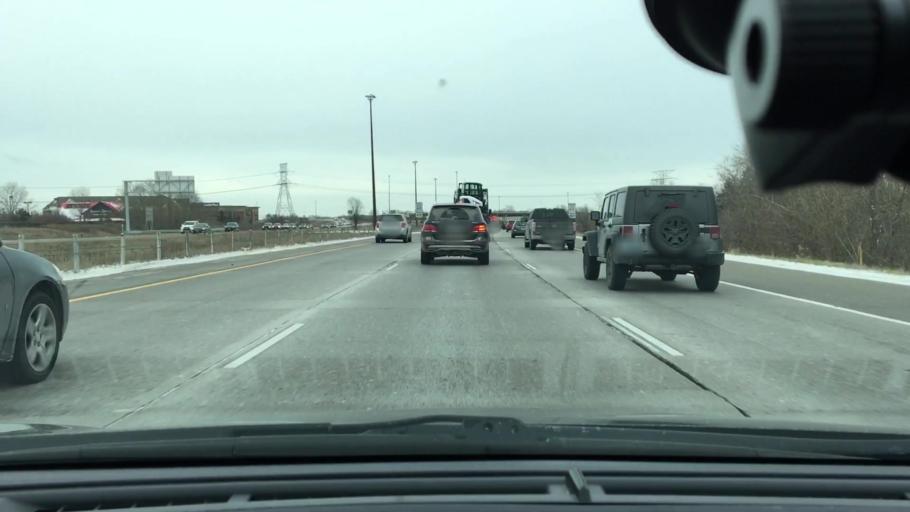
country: US
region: Minnesota
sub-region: Hennepin County
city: Maple Grove
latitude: 45.0980
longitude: -93.4524
